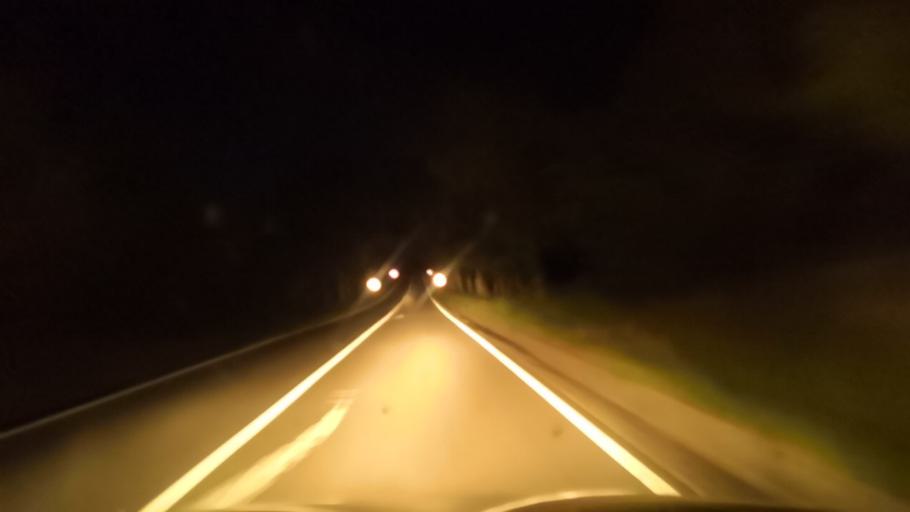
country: PT
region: Guarda
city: Alcains
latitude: 39.9702
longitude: -7.4301
